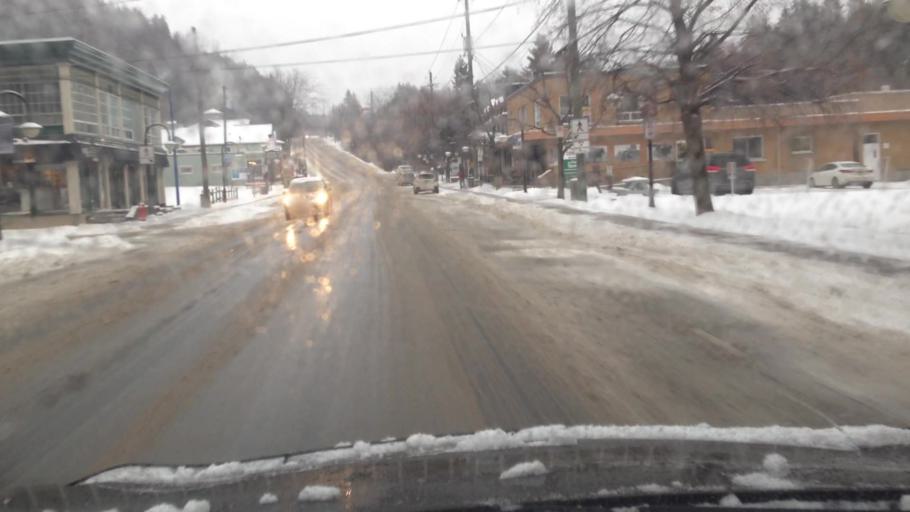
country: CA
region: Quebec
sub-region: Laurentides
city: Mont-Tremblant
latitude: 46.1187
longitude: -74.5893
